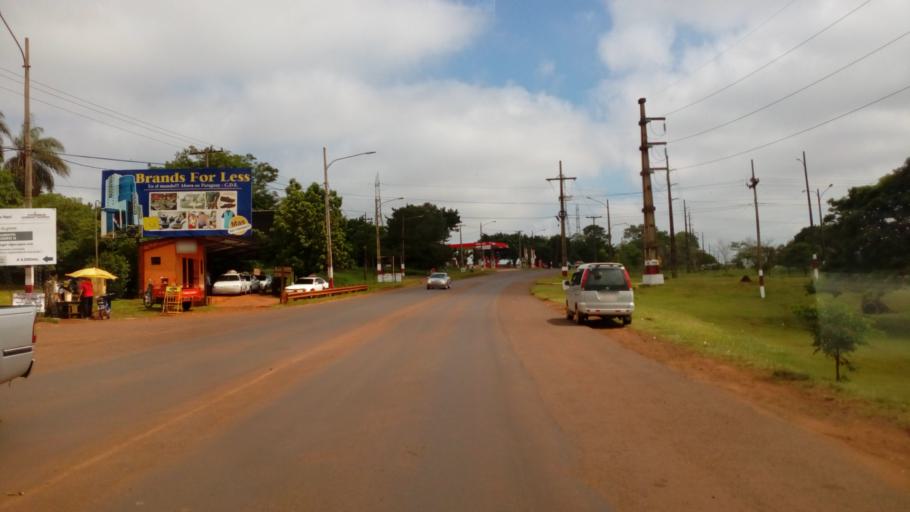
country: PY
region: Alto Parana
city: Ciudad del Este
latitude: -25.4314
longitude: -54.6388
